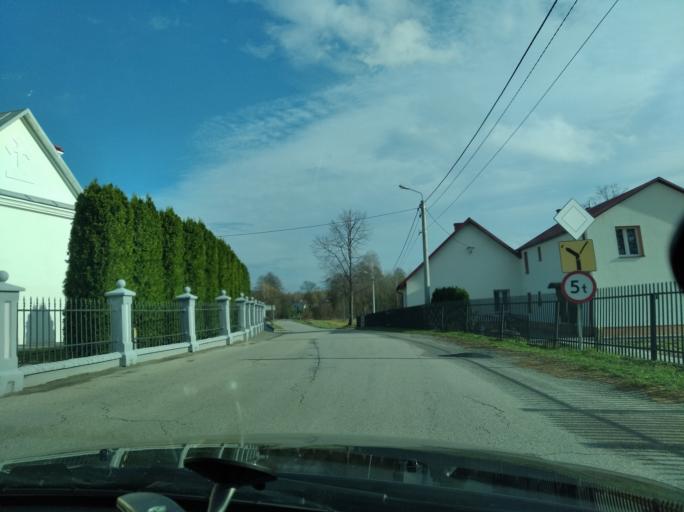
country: PL
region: Subcarpathian Voivodeship
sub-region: Powiat ropczycko-sedziszowski
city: Sedziszow Malopolski
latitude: 50.1158
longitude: 21.7344
